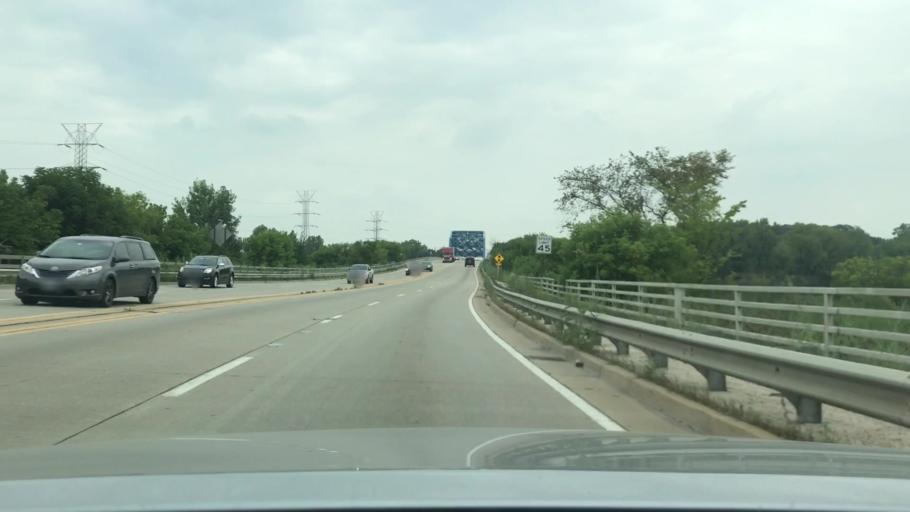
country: US
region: Illinois
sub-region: DuPage County
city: Burr Ridge
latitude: 41.6926
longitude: -87.9356
